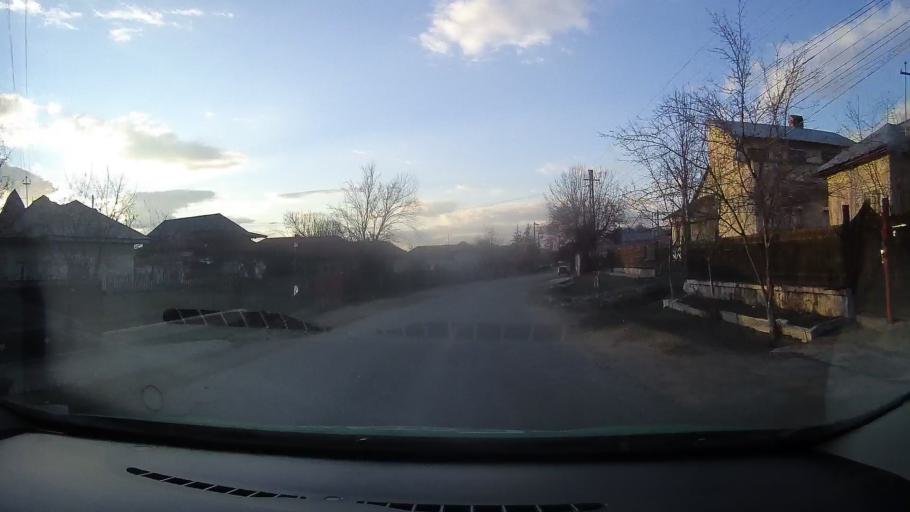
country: RO
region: Dambovita
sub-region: Comuna Gura Ocnitei
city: Adanca
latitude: 44.9209
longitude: 25.6135
